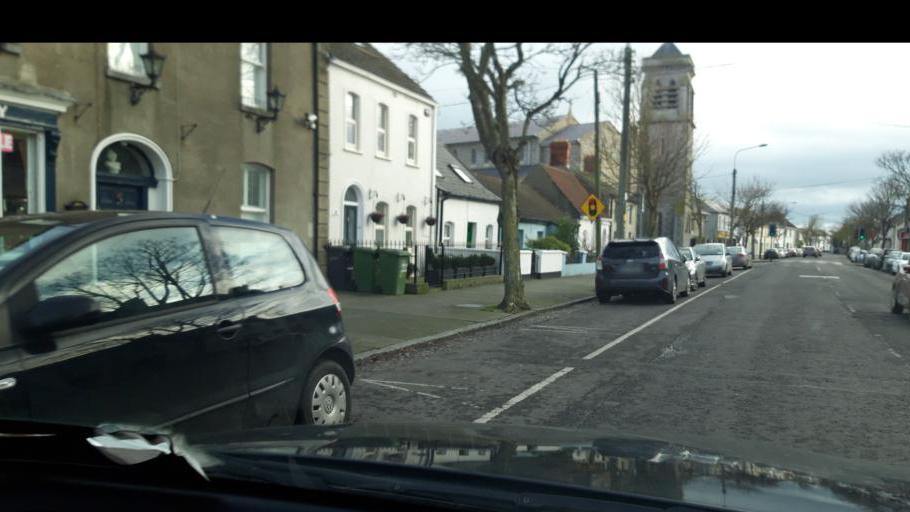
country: IE
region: Leinster
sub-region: Fingal County
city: Skerries
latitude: 53.5787
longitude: -6.1079
